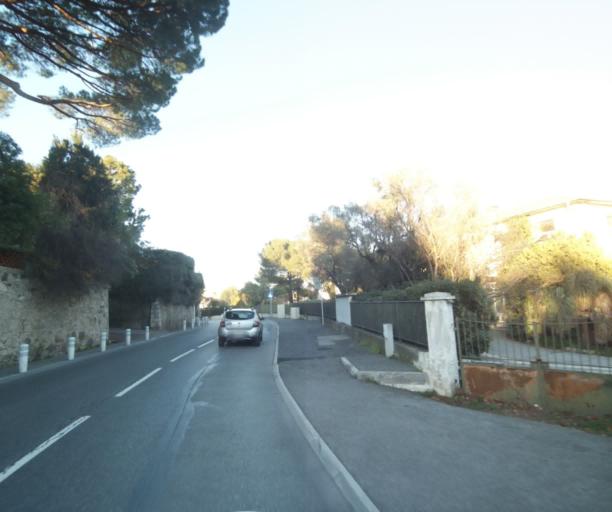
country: FR
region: Provence-Alpes-Cote d'Azur
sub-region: Departement des Alpes-Maritimes
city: Antibes
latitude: 43.5654
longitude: 7.1247
